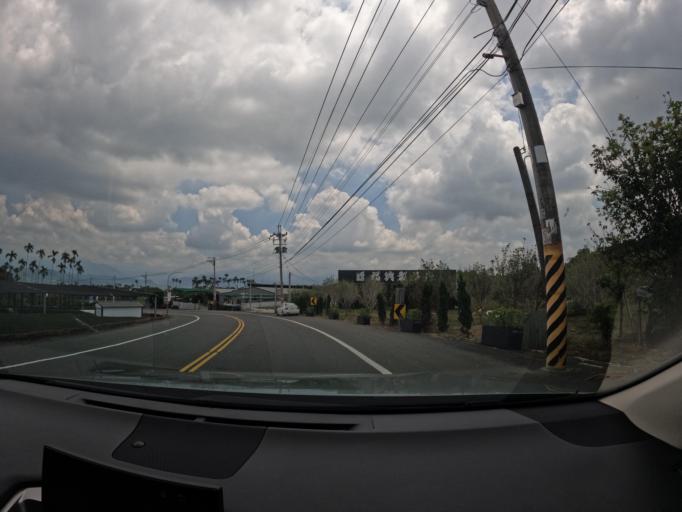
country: TW
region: Taiwan
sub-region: Nantou
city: Nantou
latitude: 23.8302
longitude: 120.6492
